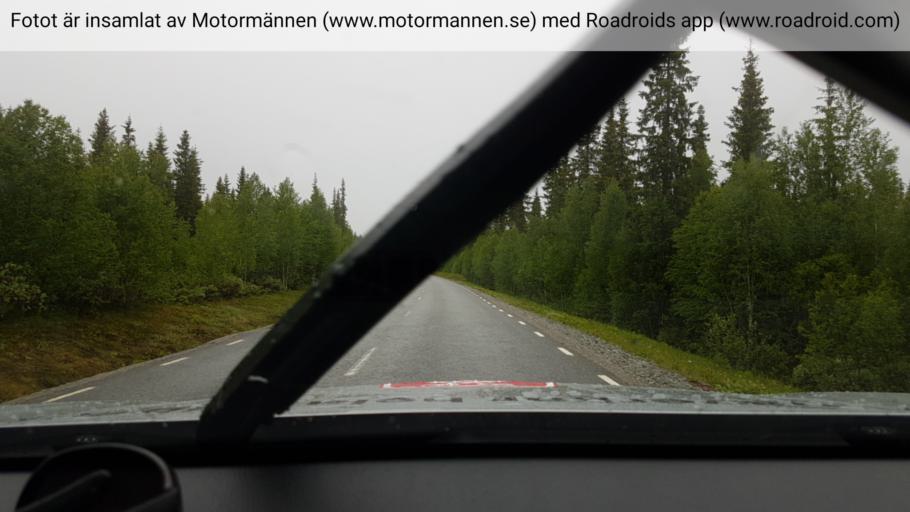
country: SE
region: Vaesterbotten
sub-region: Storumans Kommun
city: Fristad
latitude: 65.9109
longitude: 16.3110
